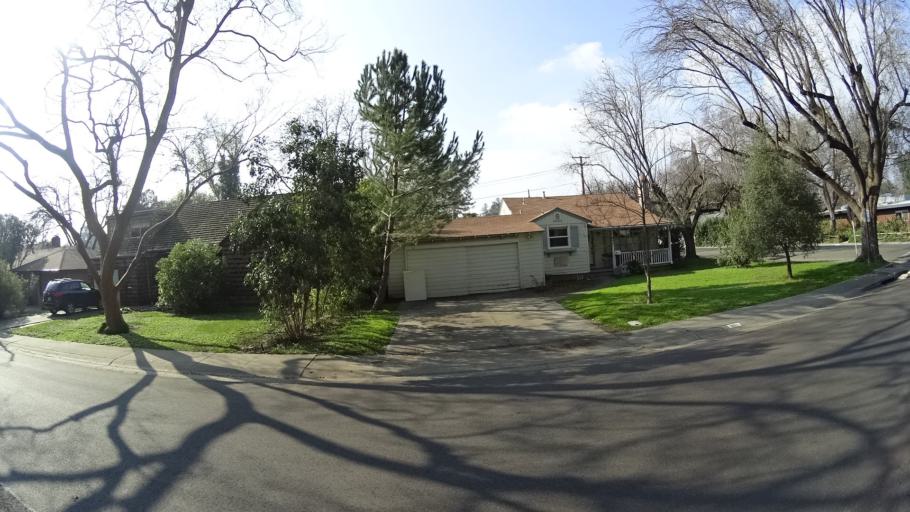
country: US
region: California
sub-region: Yolo County
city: Davis
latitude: 38.5490
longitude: -121.7478
